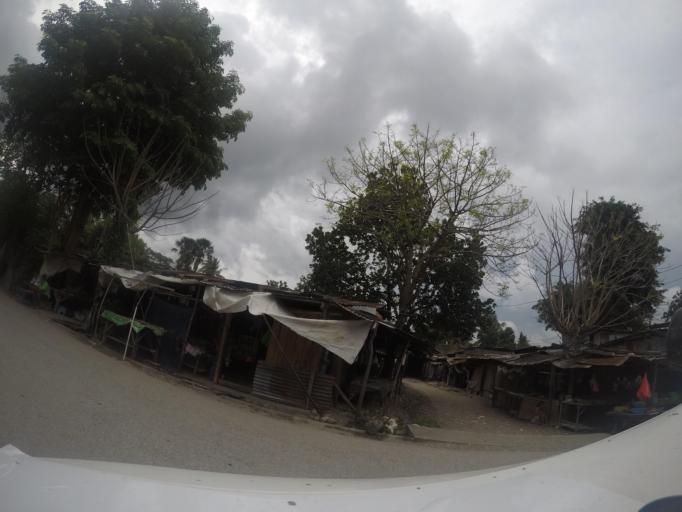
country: TL
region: Viqueque
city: Viqueque
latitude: -8.8678
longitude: 126.3677
